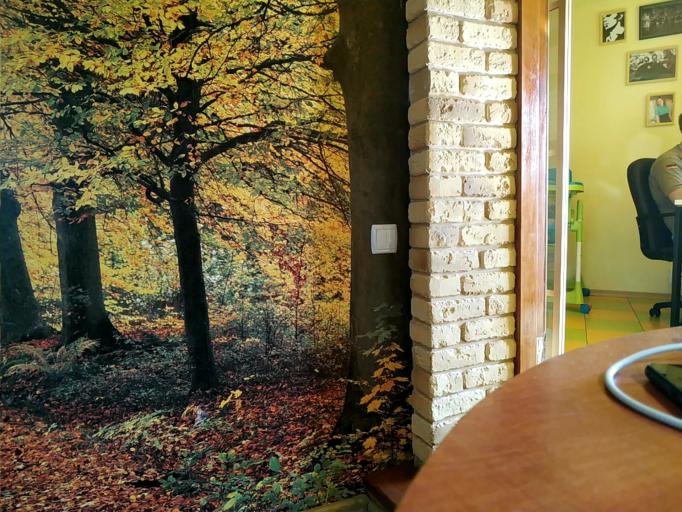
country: RU
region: Tverskaya
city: Kalashnikovo
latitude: 57.3397
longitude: 35.2814
